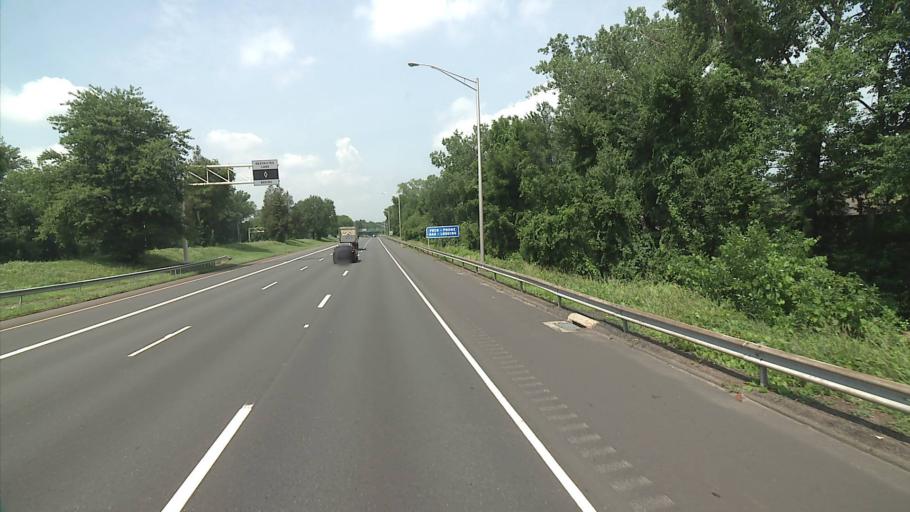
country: US
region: Connecticut
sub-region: Hartford County
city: Manchester
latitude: 41.7649
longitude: -72.5623
